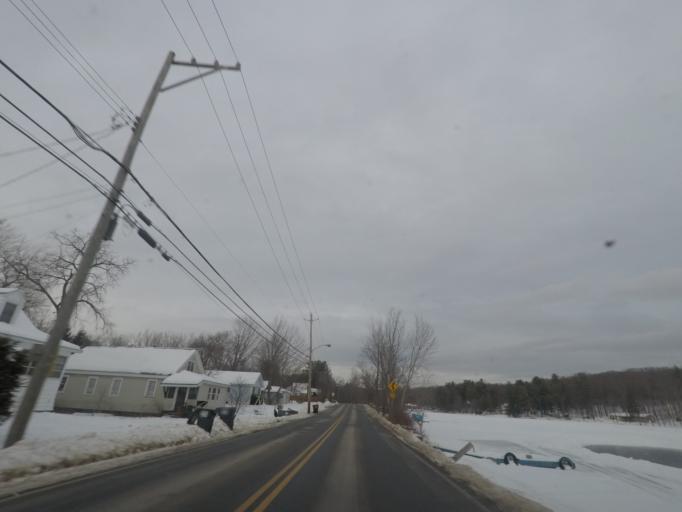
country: US
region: New York
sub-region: Rensselaer County
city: Averill Park
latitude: 42.6172
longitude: -73.5680
